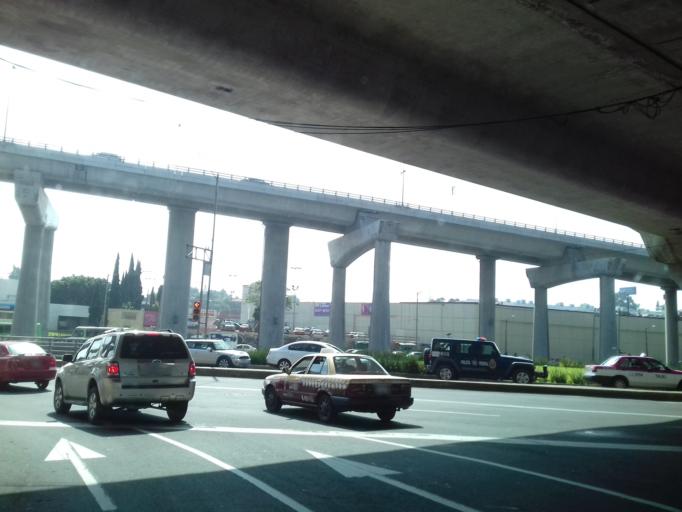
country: MX
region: Mexico City
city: Magdalena Contreras
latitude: 19.3309
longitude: -99.2113
